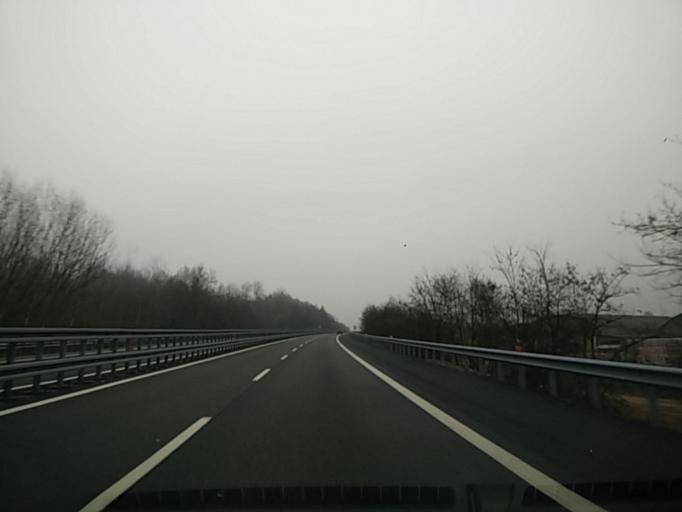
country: IT
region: Piedmont
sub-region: Provincia di Asti
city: Baldichieri d'Asti
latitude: 44.9046
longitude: 8.1026
